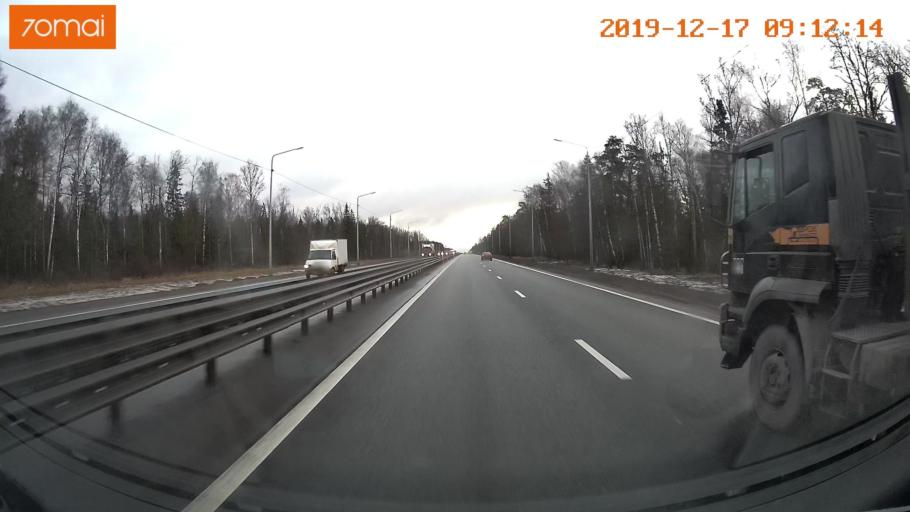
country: RU
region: Vladimir
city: Lakinsk
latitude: 55.9753
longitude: 39.8132
